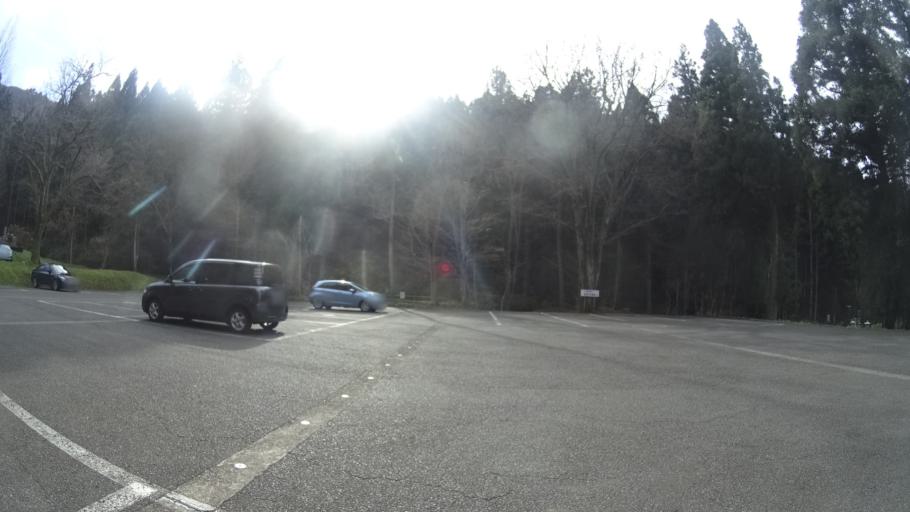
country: JP
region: Niigata
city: Muikamachi
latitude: 37.0309
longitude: 138.8893
